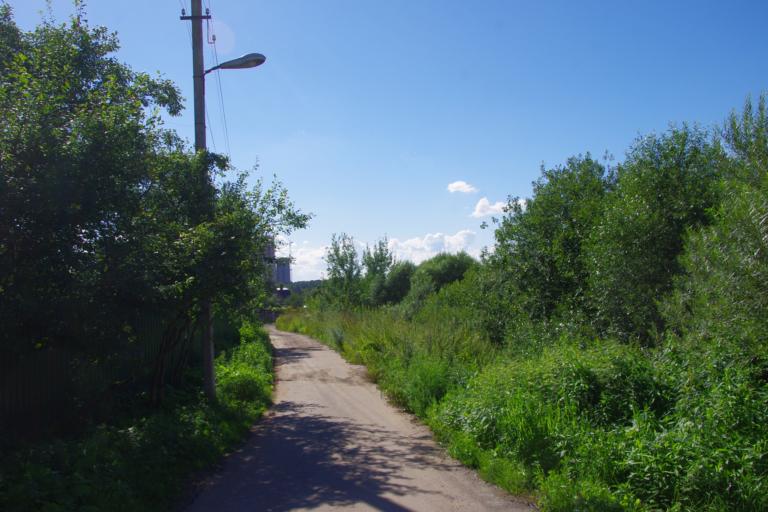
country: RU
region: Moskovskaya
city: Opalikha
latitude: 55.8375
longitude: 37.2902
